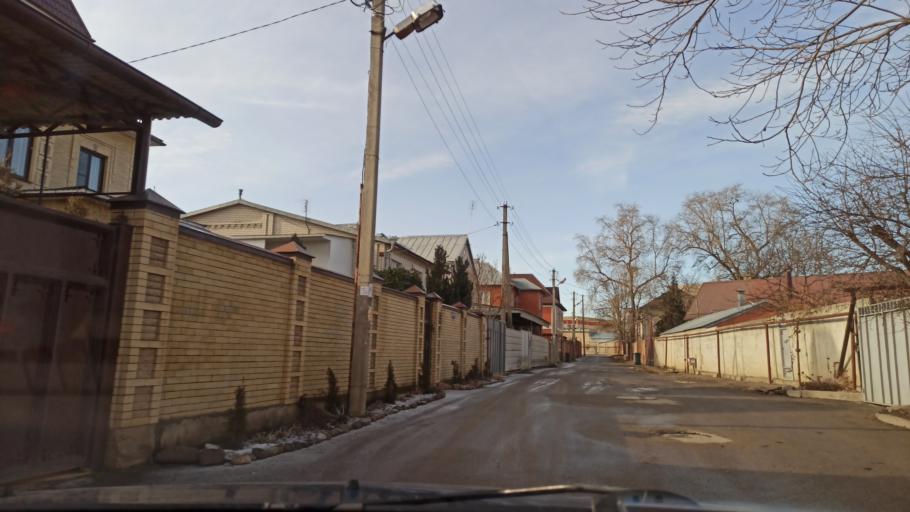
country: RU
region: Stavropol'skiy
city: Yessentukskaya
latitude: 44.0372
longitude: 42.8767
